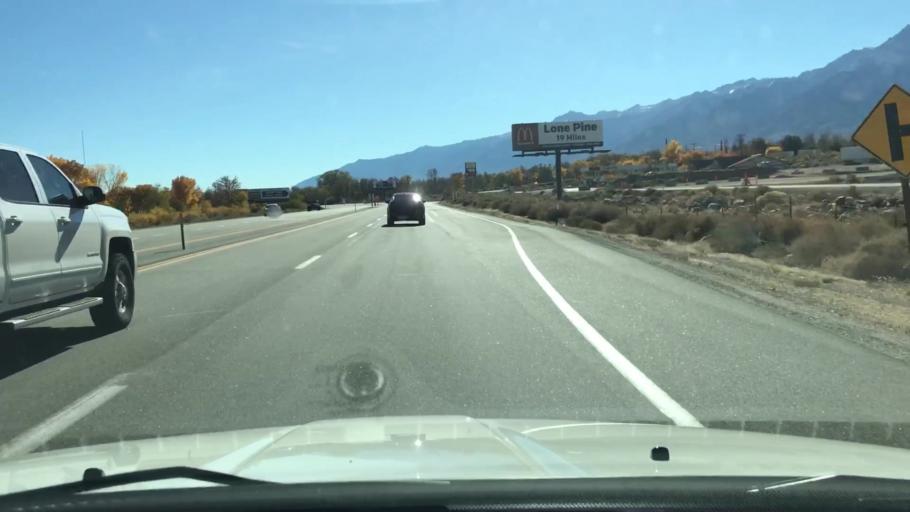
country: US
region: California
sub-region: Inyo County
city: Lone Pine
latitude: 36.8386
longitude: -118.2292
